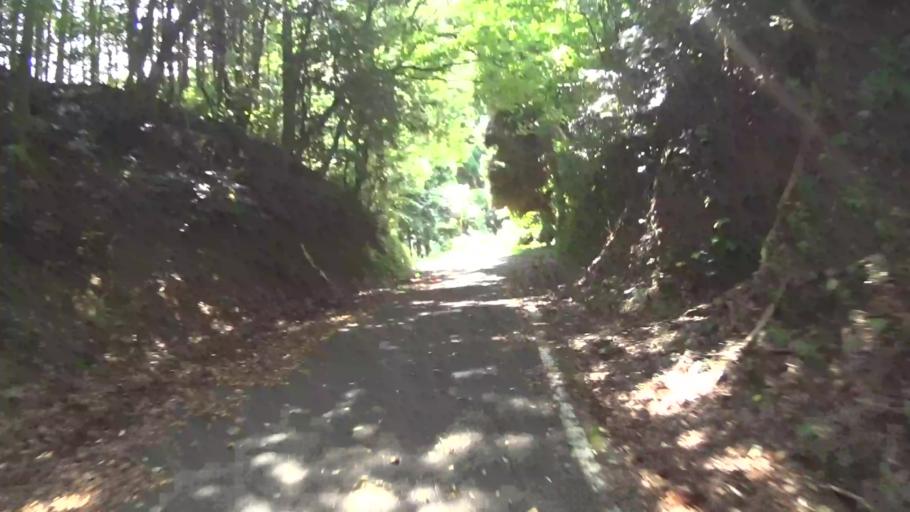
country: JP
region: Kyoto
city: Miyazu
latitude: 35.6553
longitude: 135.2430
